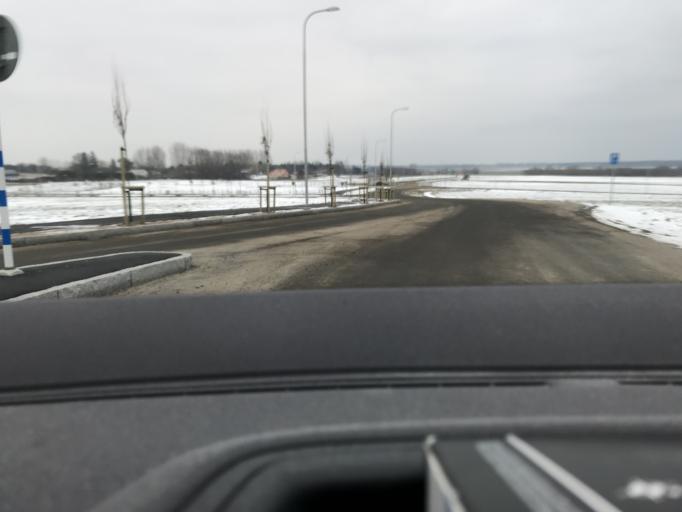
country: SE
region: Skane
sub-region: Ystads Kommun
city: Ystad
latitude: 55.4546
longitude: 13.8500
